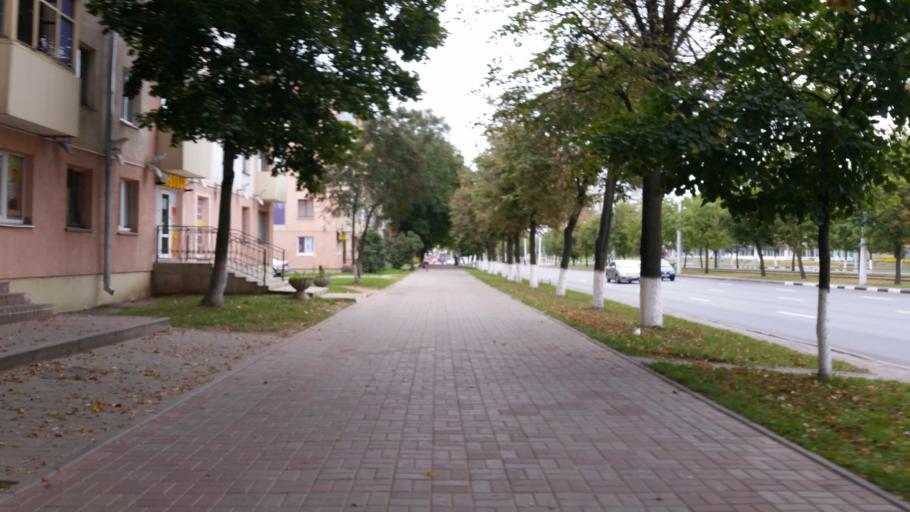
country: BY
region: Vitebsk
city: Vitebsk
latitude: 55.1821
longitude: 30.2077
